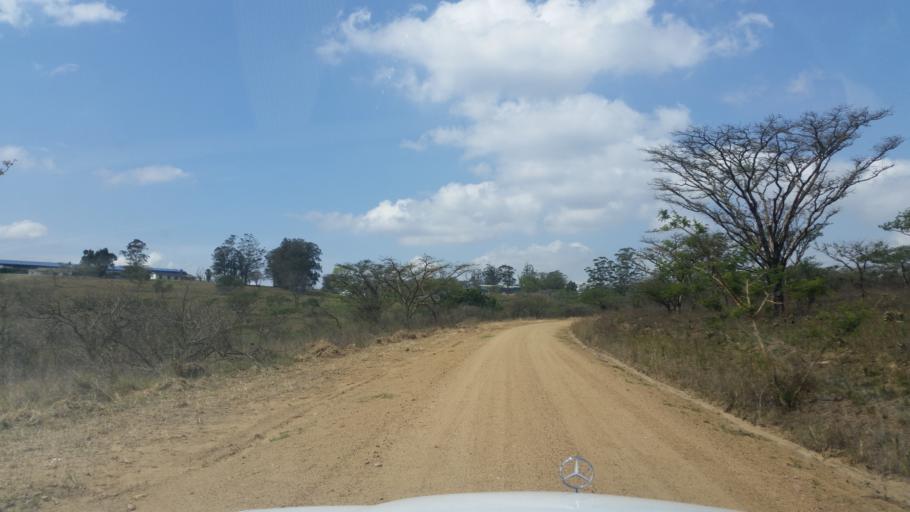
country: ZA
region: KwaZulu-Natal
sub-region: uMgungundlovu District Municipality
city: Camperdown
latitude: -29.7044
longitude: 30.4857
